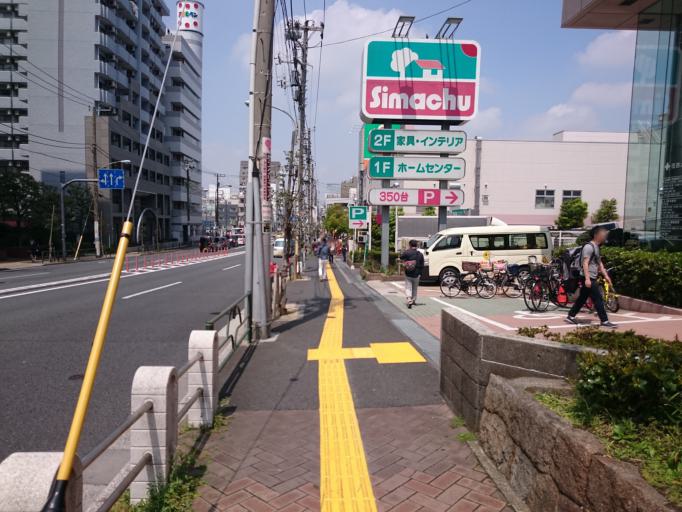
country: JP
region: Tokyo
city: Urayasu
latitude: 35.6853
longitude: 139.8161
